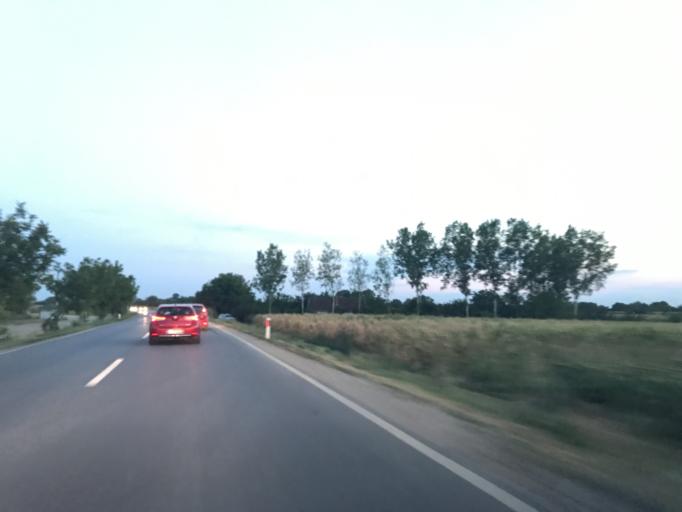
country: RS
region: Central Serbia
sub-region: Branicevski Okrug
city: Pozarevac
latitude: 44.6293
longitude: 21.1445
